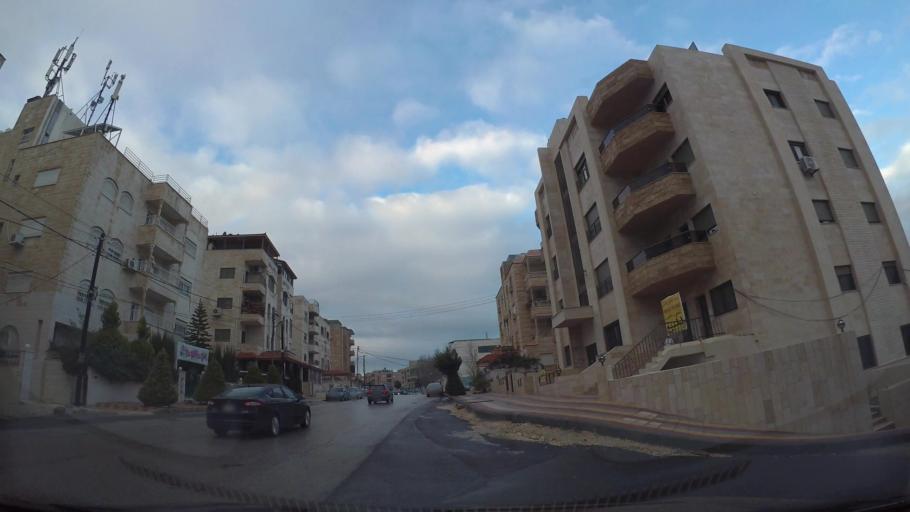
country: JO
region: Amman
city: Amman
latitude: 31.9804
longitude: 35.9150
